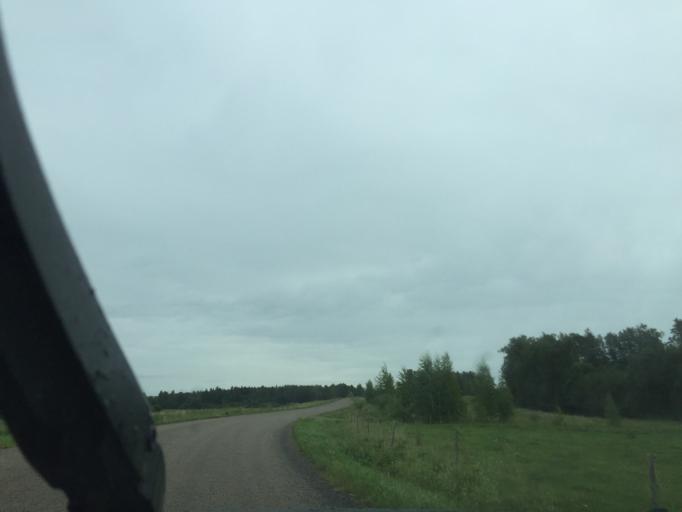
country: LV
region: Livani
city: Livani
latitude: 56.4485
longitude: 26.2743
